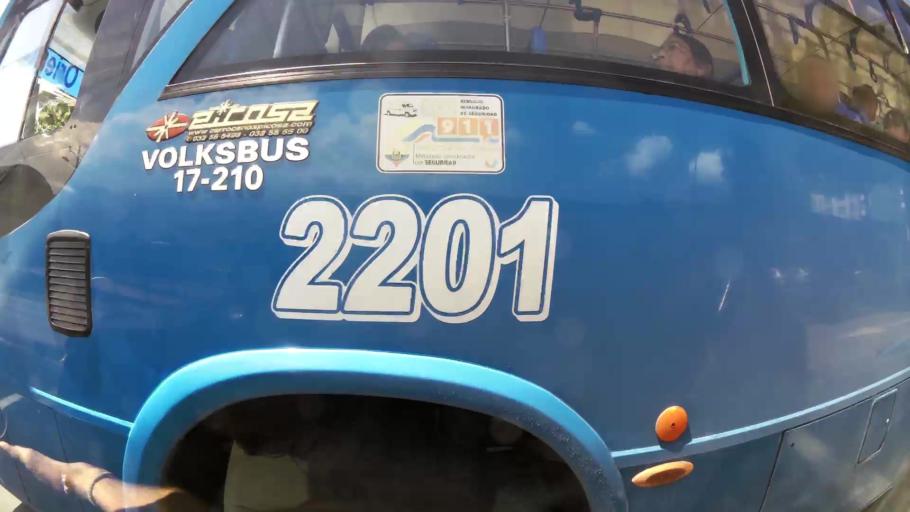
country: EC
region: Pichincha
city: Quito
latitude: -0.2643
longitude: -78.5250
